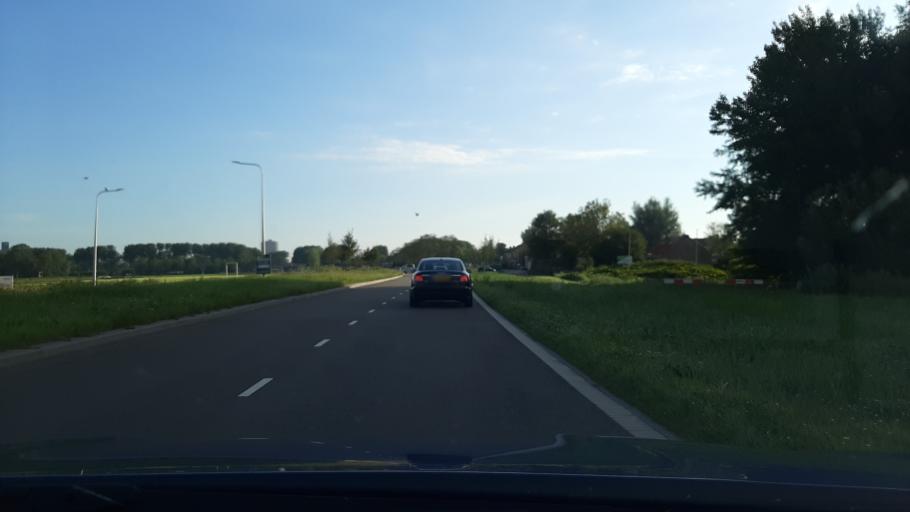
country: NL
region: Friesland
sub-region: Gemeente Leeuwarden
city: Goutum
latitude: 53.1736
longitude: 5.7929
